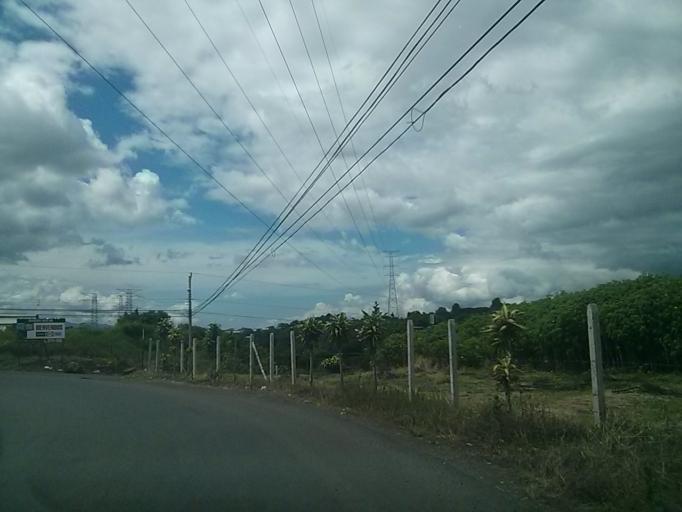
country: CR
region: Heredia
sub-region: Canton de Belen
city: San Antonio
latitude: 9.9662
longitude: -84.1956
